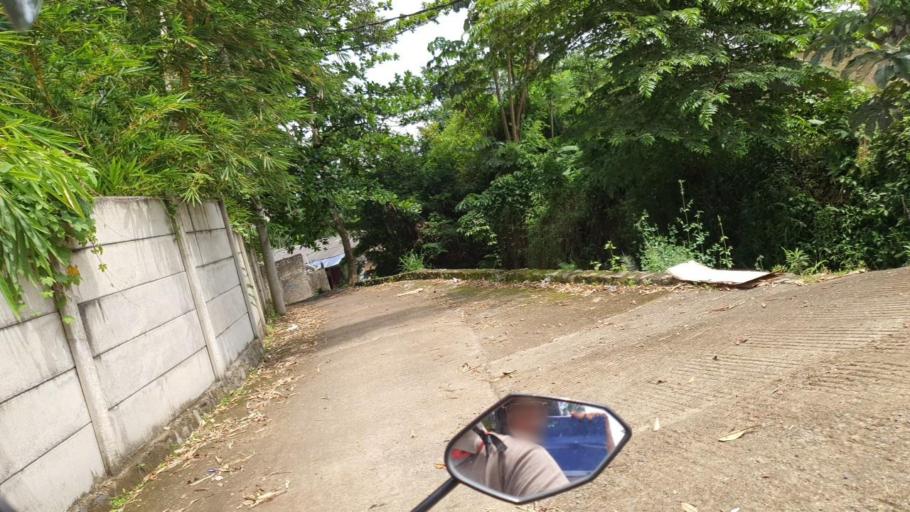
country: ID
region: West Java
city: Caringin
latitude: -6.6528
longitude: 106.8974
